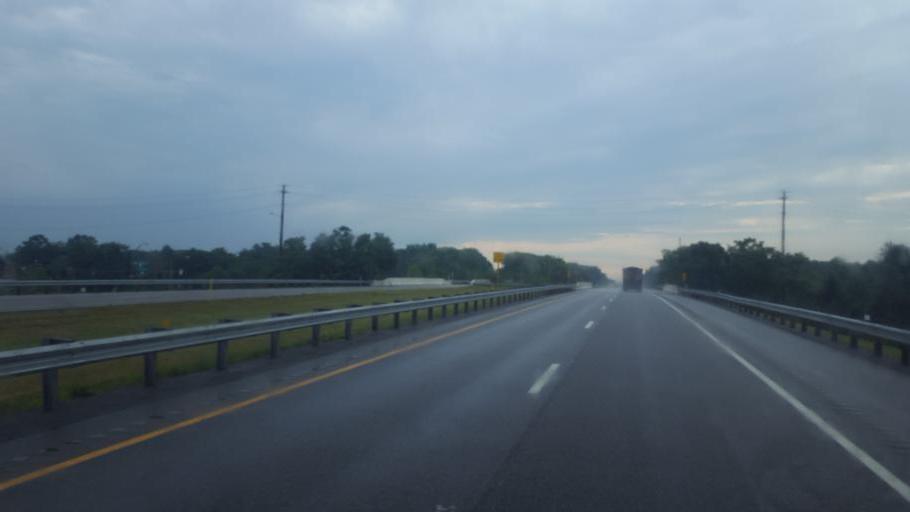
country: US
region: Ohio
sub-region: Geauga County
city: Bainbridge
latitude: 41.3877
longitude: -81.3407
